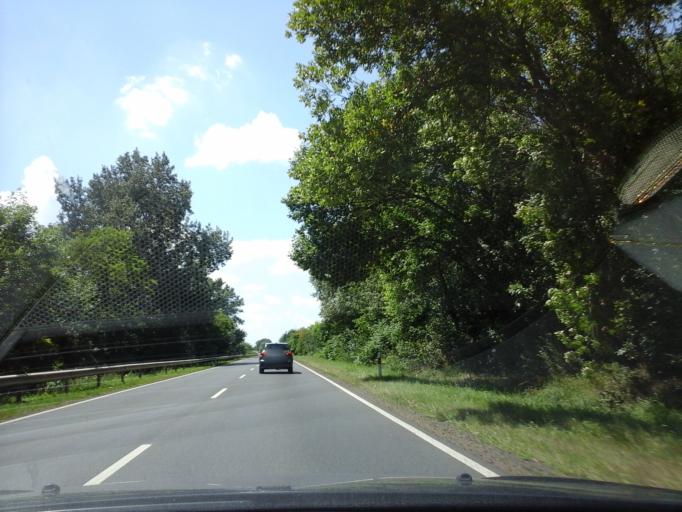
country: HU
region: Hajdu-Bihar
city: Ebes
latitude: 47.4682
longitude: 21.4612
